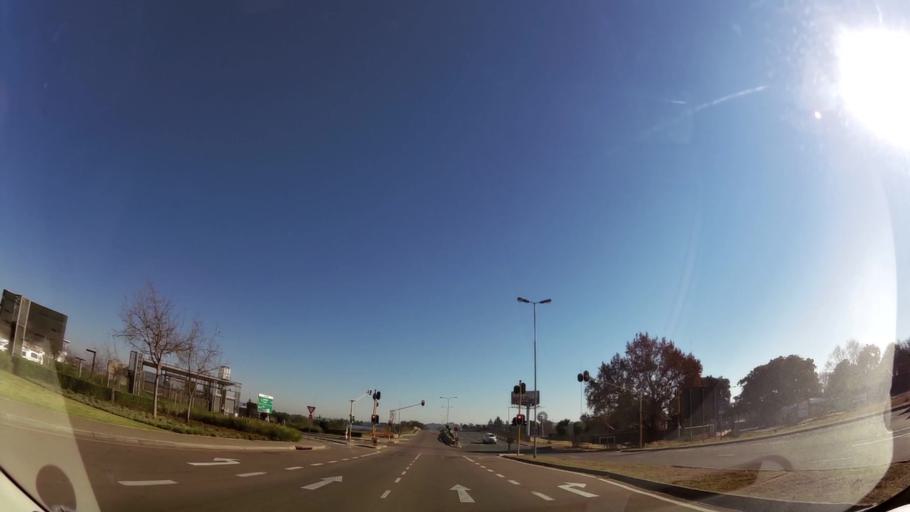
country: ZA
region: Gauteng
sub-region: City of Tshwane Metropolitan Municipality
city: Centurion
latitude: -25.8633
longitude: 28.2103
